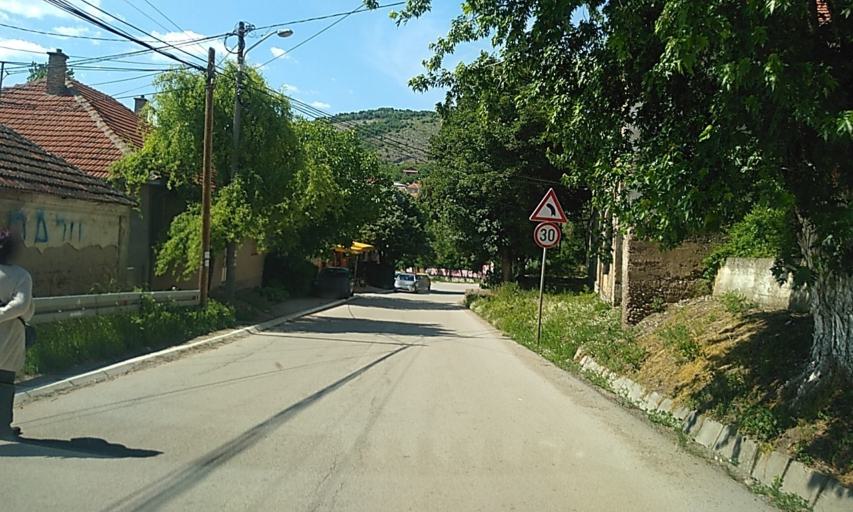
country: RS
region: Central Serbia
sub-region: Nisavski Okrug
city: Nis
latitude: 43.3641
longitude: 21.9675
